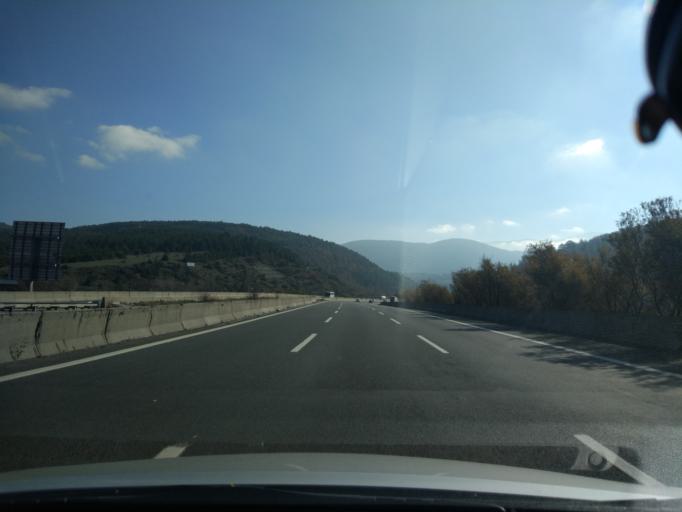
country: TR
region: Bolu
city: Bolu
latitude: 40.7521
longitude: 31.7762
